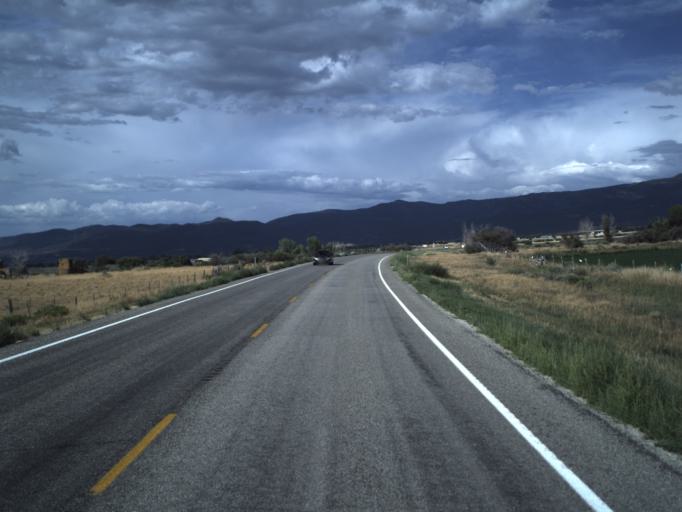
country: US
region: Utah
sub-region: Sanpete County
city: Mount Pleasant
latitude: 39.5126
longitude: -111.4937
